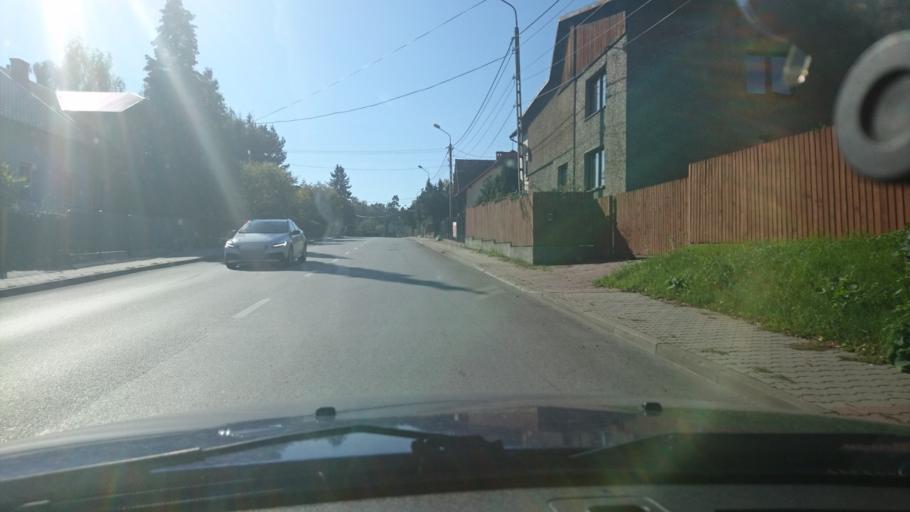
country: PL
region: Silesian Voivodeship
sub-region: Powiat bielski
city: Czechowice-Dziedzice
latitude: 49.9026
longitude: 19.0031
